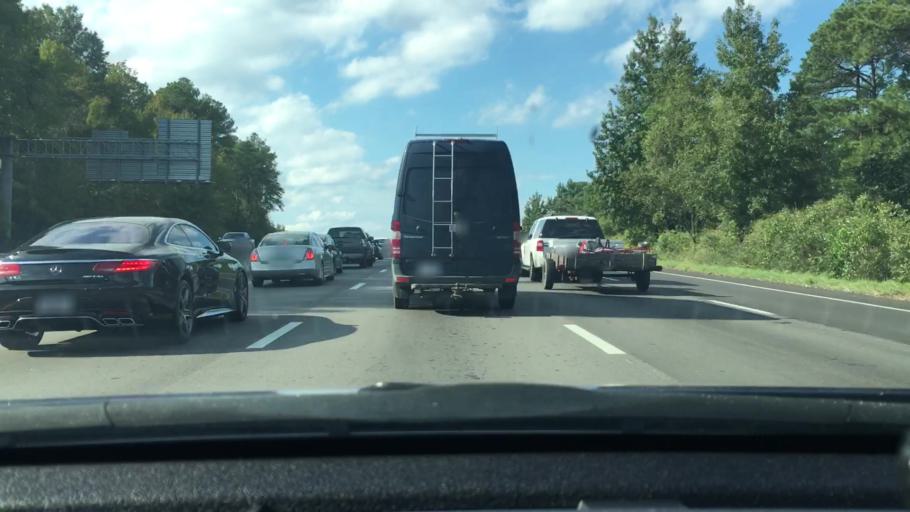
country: US
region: South Carolina
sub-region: Lexington County
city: Saint Andrews
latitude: 34.0460
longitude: -81.1192
